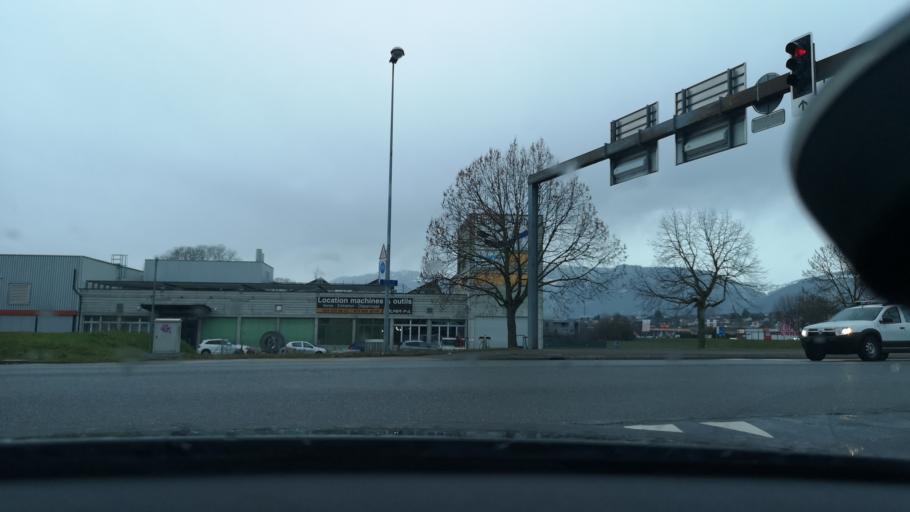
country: CH
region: Vaud
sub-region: Jura-Nord vaudois District
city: Yverdon-les-Bains
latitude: 46.7885
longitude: 6.6305
